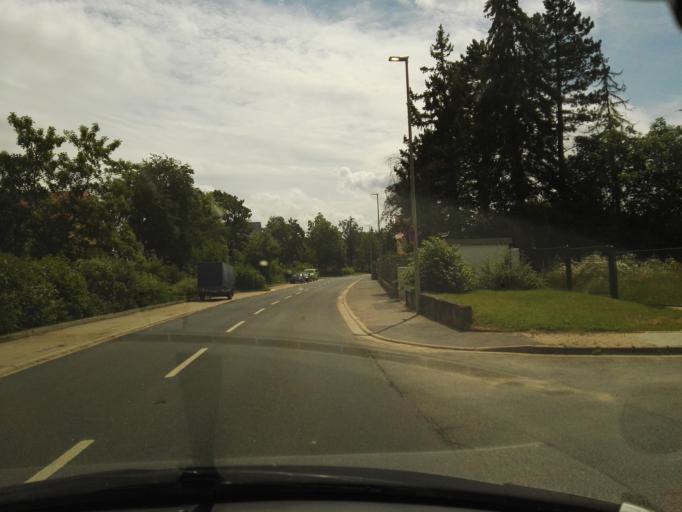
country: DE
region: Bavaria
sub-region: Upper Franconia
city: Altenkunstadt
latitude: 50.1315
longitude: 11.2454
